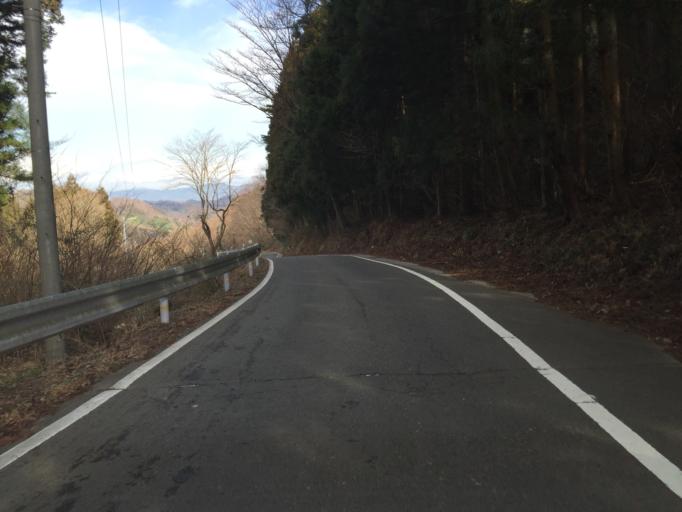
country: JP
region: Fukushima
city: Fukushima-shi
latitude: 37.7138
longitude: 140.5515
